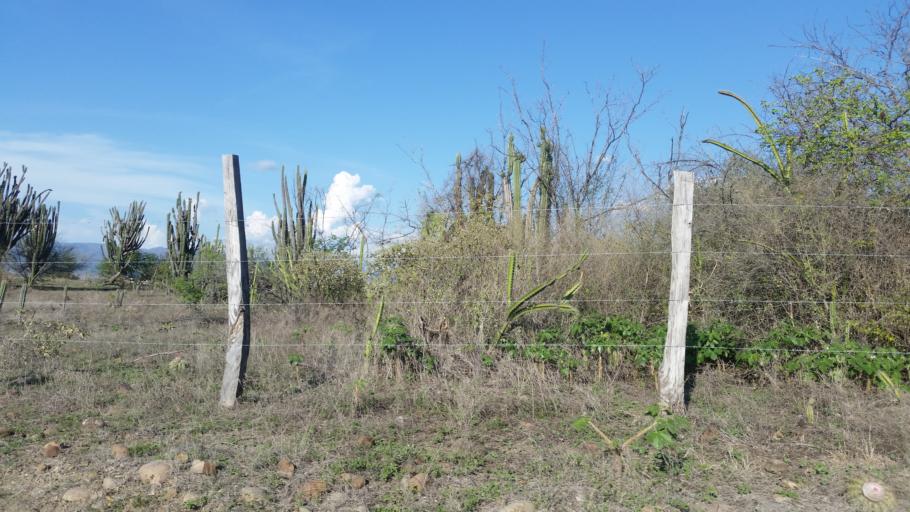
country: CO
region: Huila
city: Villavieja
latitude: 3.2309
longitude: -75.1529
